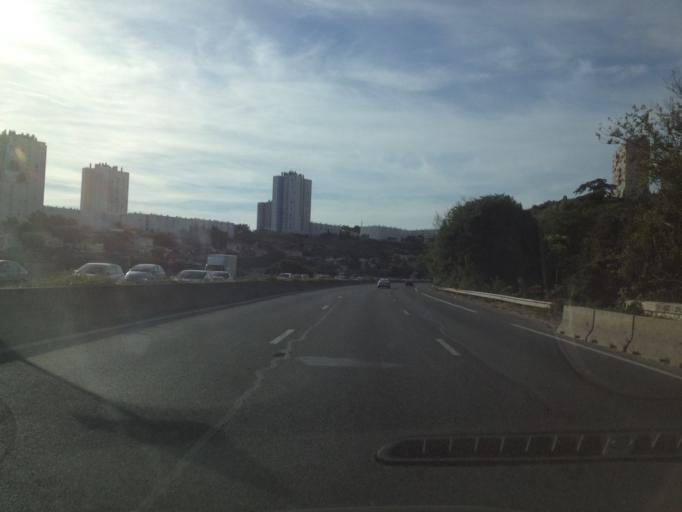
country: FR
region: Provence-Alpes-Cote d'Azur
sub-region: Departement des Bouches-du-Rhone
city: Marseille 14
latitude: 43.3527
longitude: 5.3657
